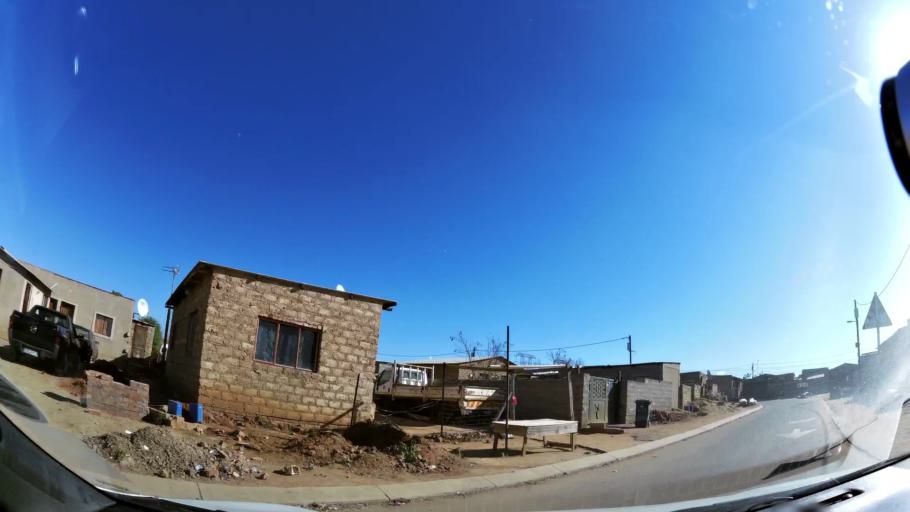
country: ZA
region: Gauteng
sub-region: City of Johannesburg Metropolitan Municipality
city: Diepsloot
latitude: -25.9062
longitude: 28.0930
